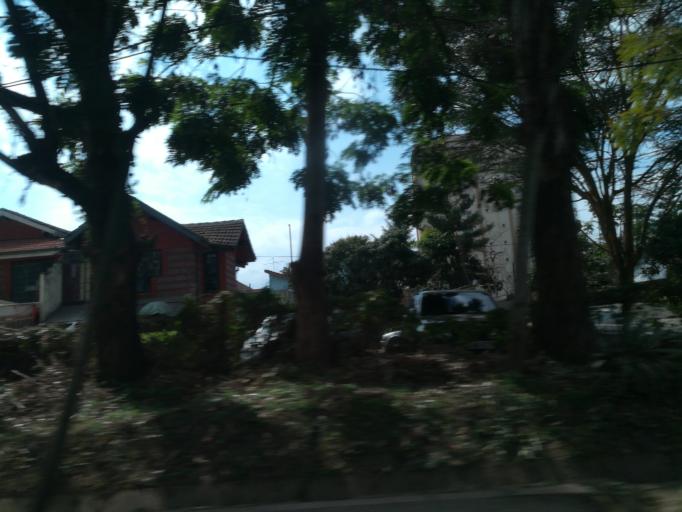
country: KE
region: Nairobi Area
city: Nairobi
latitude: -1.2890
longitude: 36.7889
